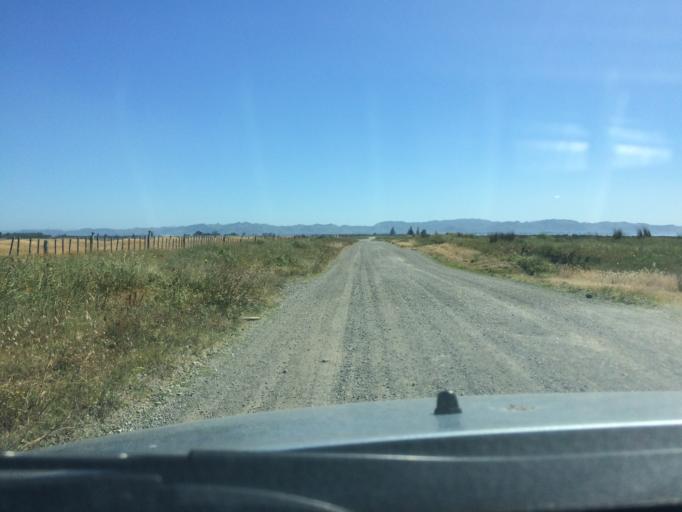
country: NZ
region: Gisborne
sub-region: Gisborne District
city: Gisborne
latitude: -38.7047
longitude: 177.9459
